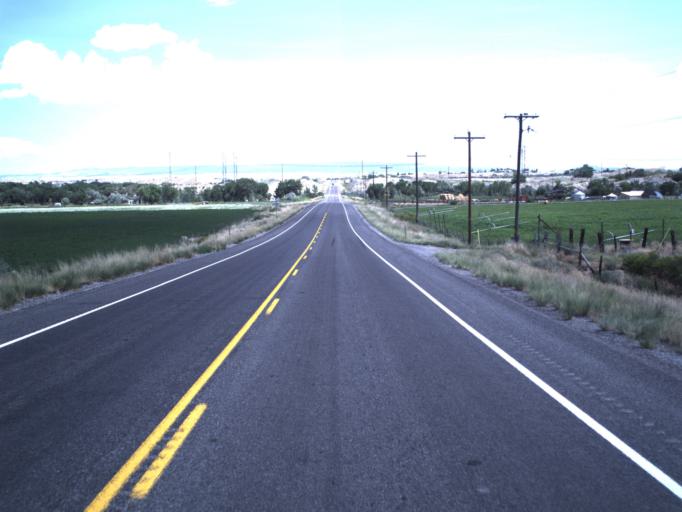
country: US
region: Utah
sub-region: Emery County
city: Huntington
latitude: 39.3495
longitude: -110.9983
